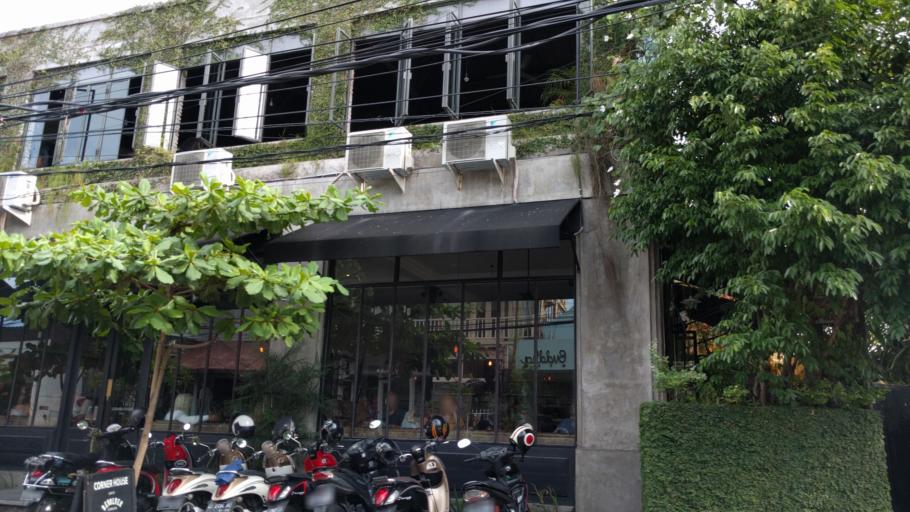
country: ID
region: Bali
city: Kuta
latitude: -8.6835
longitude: 115.1644
